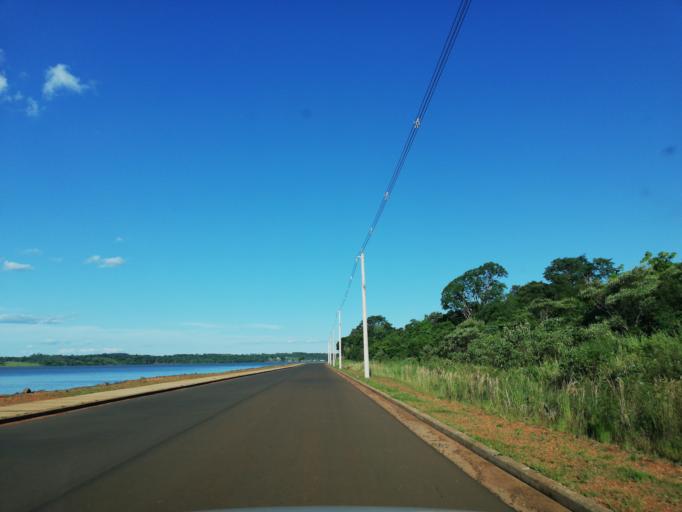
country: AR
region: Misiones
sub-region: Departamento de Candelaria
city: Candelaria
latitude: -27.4509
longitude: -55.7798
